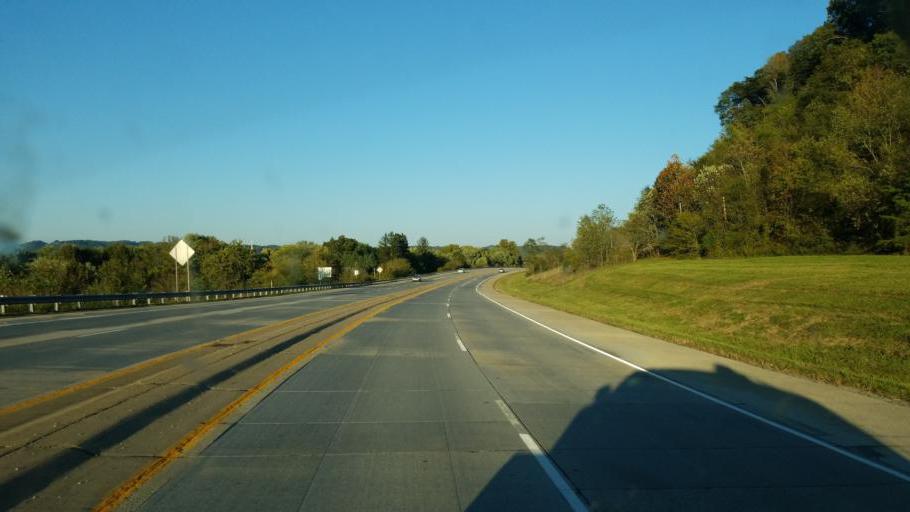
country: US
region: Ohio
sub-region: Scioto County
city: Portsmouth
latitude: 38.7237
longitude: -83.0144
